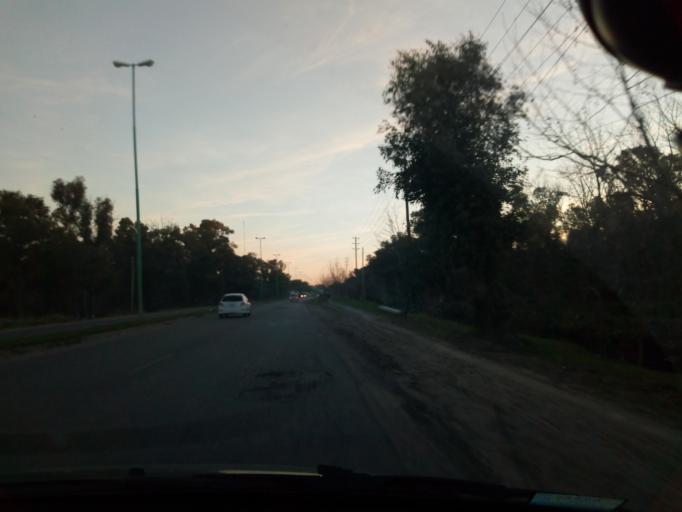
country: AR
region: Buenos Aires
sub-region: Partido de Ensenada
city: Ensenada
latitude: -34.8813
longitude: -57.9243
